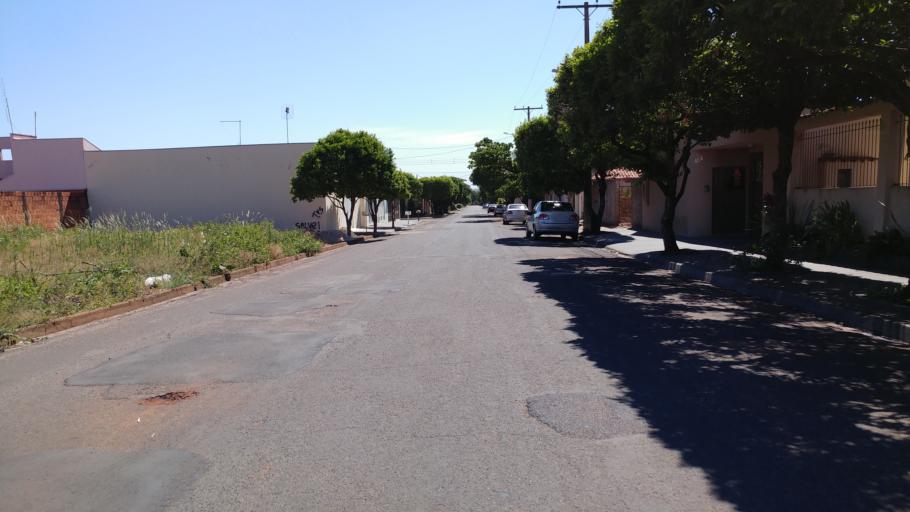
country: BR
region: Sao Paulo
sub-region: Paraguacu Paulista
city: Paraguacu Paulista
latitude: -22.4131
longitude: -50.5899
